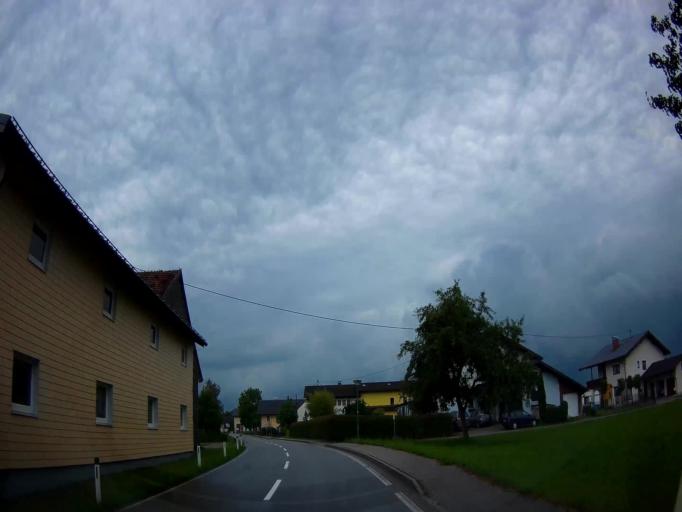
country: AT
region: Salzburg
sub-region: Politischer Bezirk Salzburg-Umgebung
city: Mattsee
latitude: 48.0588
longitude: 13.1512
